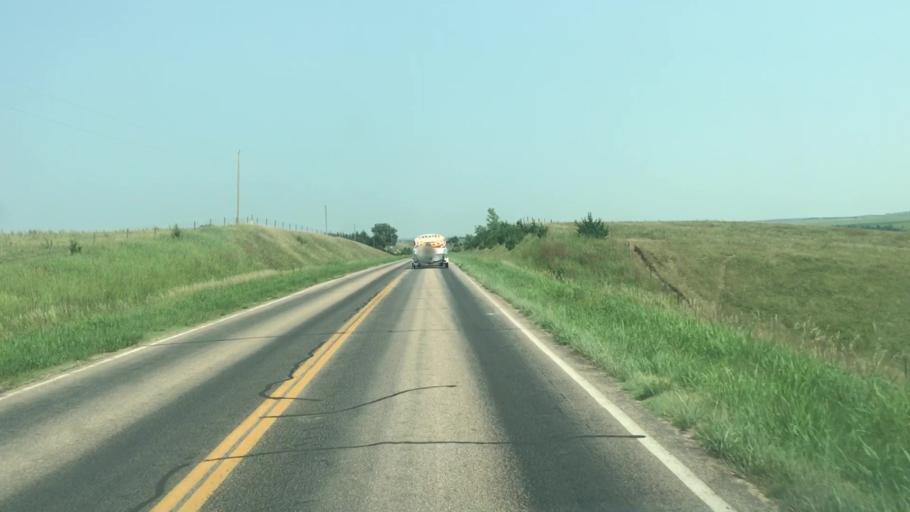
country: US
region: Nebraska
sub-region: Sherman County
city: Loup City
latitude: 41.2791
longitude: -98.9052
